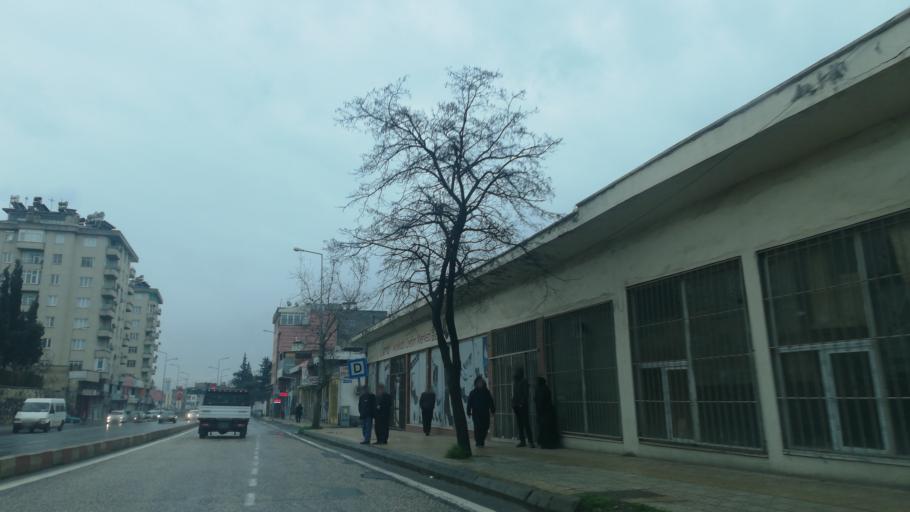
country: TR
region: Kahramanmaras
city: Kahramanmaras
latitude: 37.5729
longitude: 36.9398
